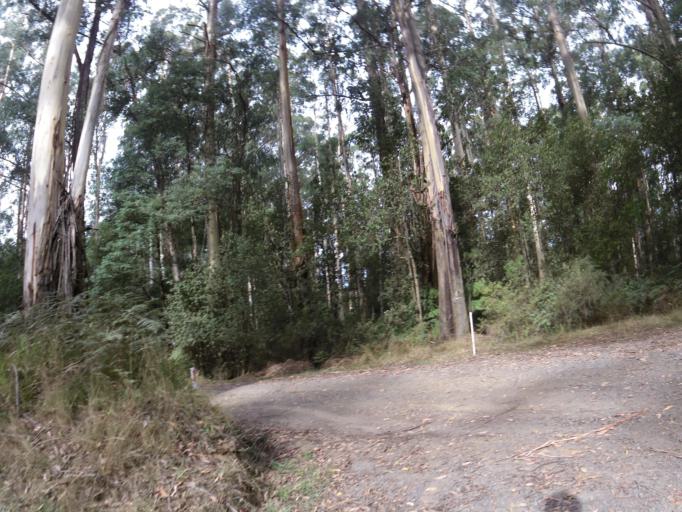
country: AU
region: Victoria
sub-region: Baw Baw
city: Warragul
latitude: -37.8964
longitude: 145.9626
